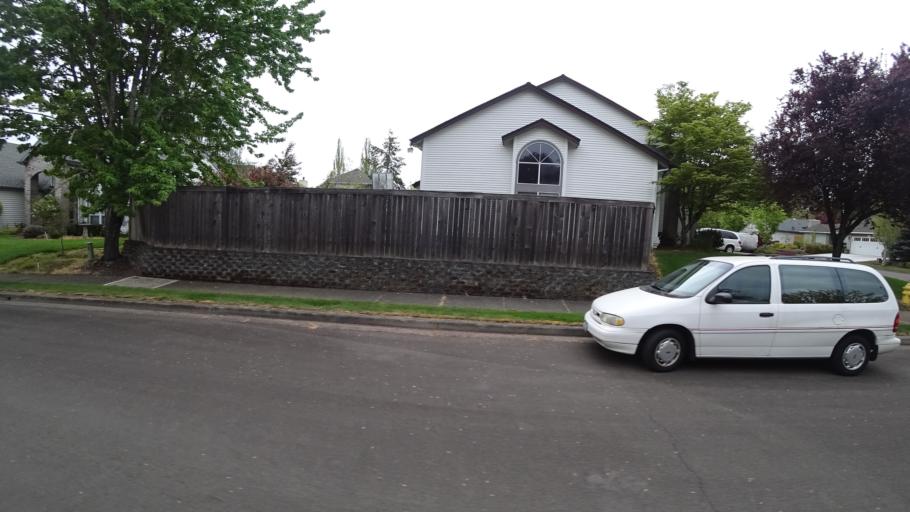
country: US
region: Oregon
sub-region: Washington County
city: Hillsboro
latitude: 45.5481
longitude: -122.9866
